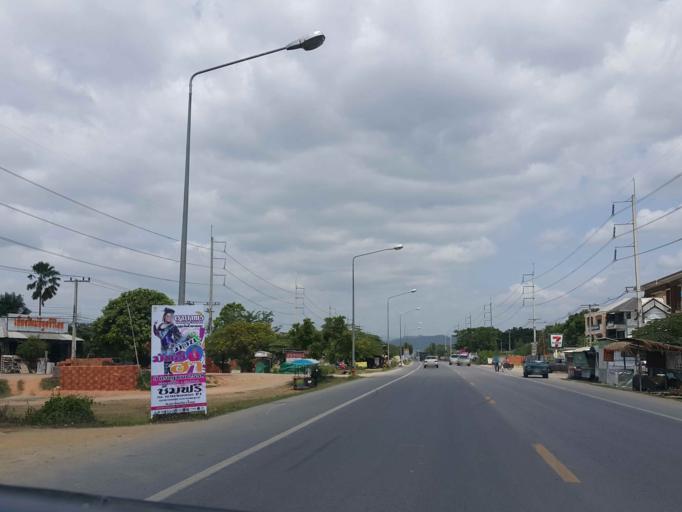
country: TH
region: Chiang Mai
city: Hang Dong
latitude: 18.7218
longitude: 98.9564
